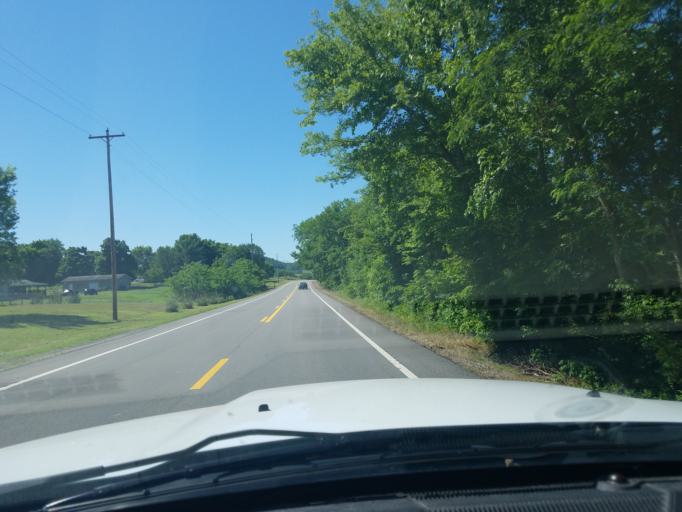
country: US
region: Tennessee
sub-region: Sumner County
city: Westmoreland
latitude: 36.4605
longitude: -86.2683
